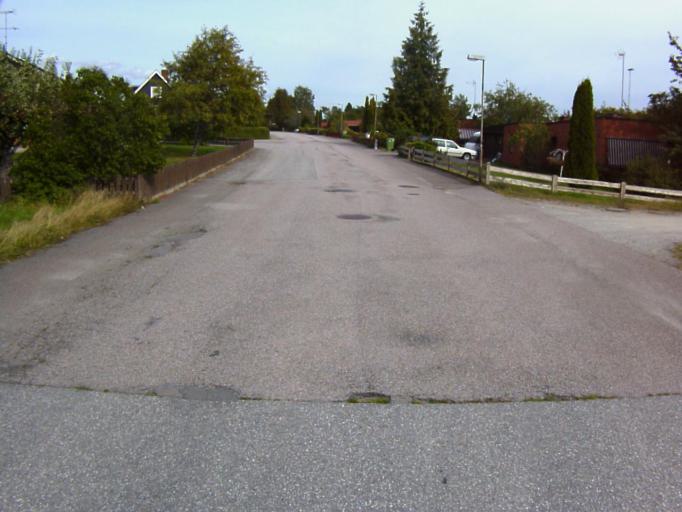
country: SE
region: Soedermanland
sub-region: Eskilstuna Kommun
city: Arla
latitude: 59.3855
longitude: 16.6776
